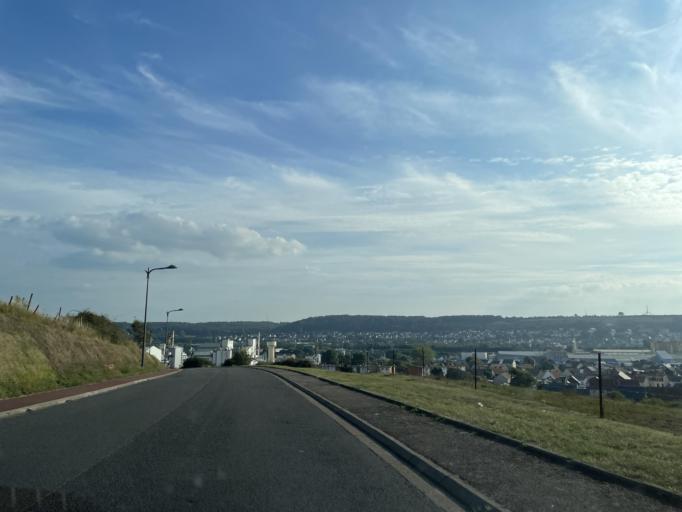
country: FR
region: Picardie
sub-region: Departement de la Somme
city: Mers-les-Bains
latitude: 50.0677
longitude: 1.3925
